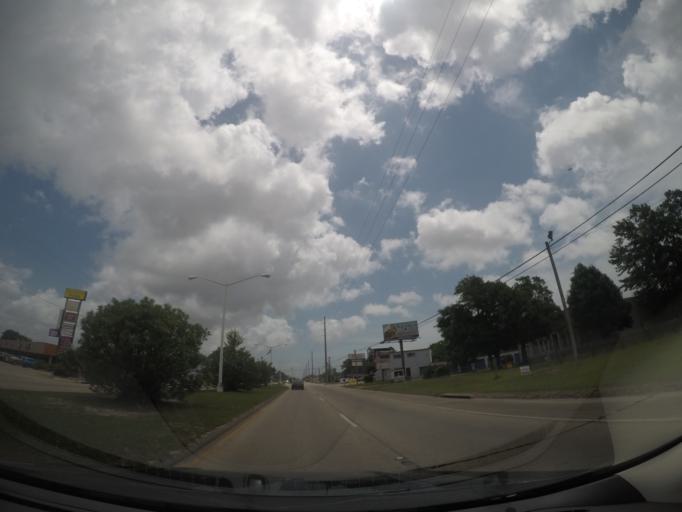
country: US
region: Mississippi
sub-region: Hancock County
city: Waveland
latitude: 30.3076
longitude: -89.3736
